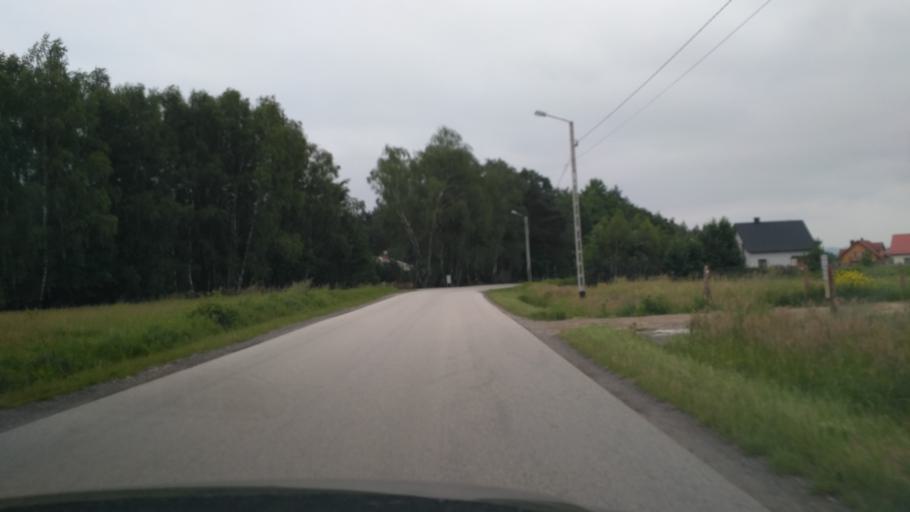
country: PL
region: Subcarpathian Voivodeship
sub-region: Powiat ropczycko-sedziszowski
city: Sedziszow Malopolski
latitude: 50.1162
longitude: 21.6743
